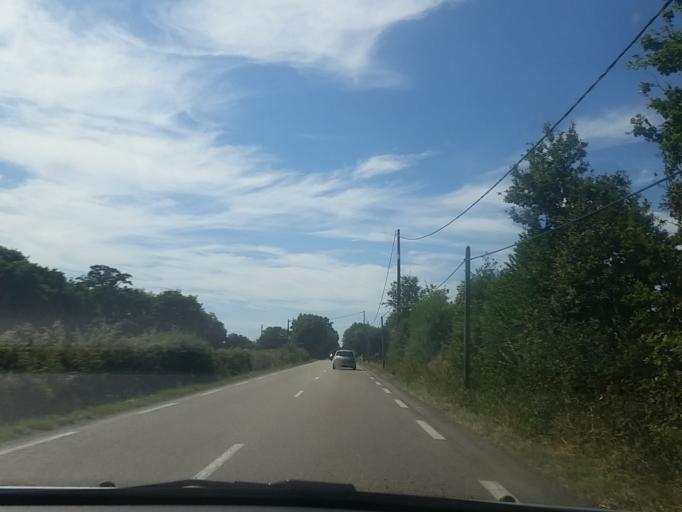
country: FR
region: Pays de la Loire
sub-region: Departement de la Loire-Atlantique
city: Chauve
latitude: 47.1850
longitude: -1.9690
